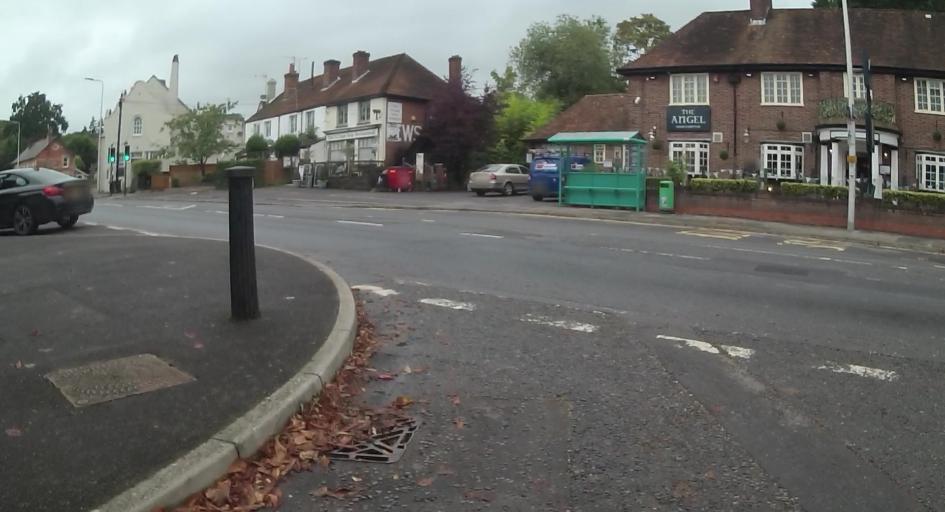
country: GB
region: England
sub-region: Hampshire
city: Tadley
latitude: 51.3973
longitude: -1.1774
